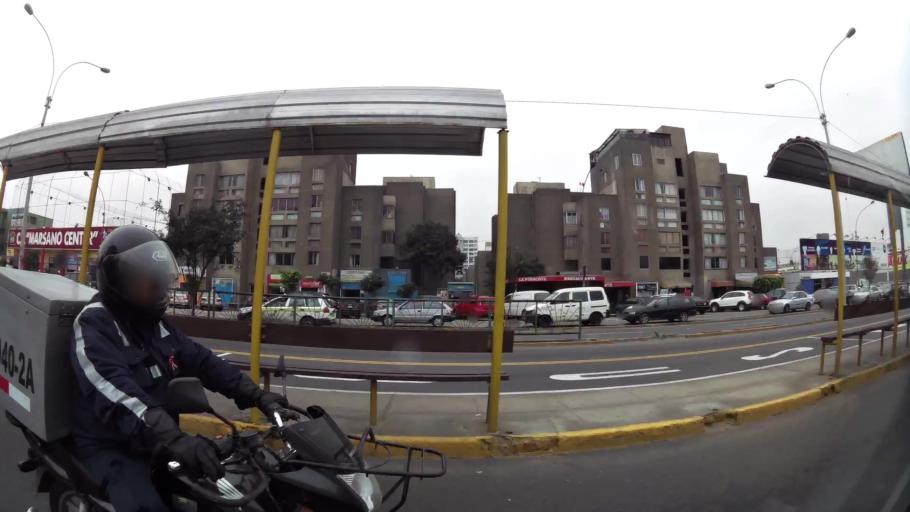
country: PE
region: Lima
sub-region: Lima
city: Surco
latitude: -12.1172
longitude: -77.0090
